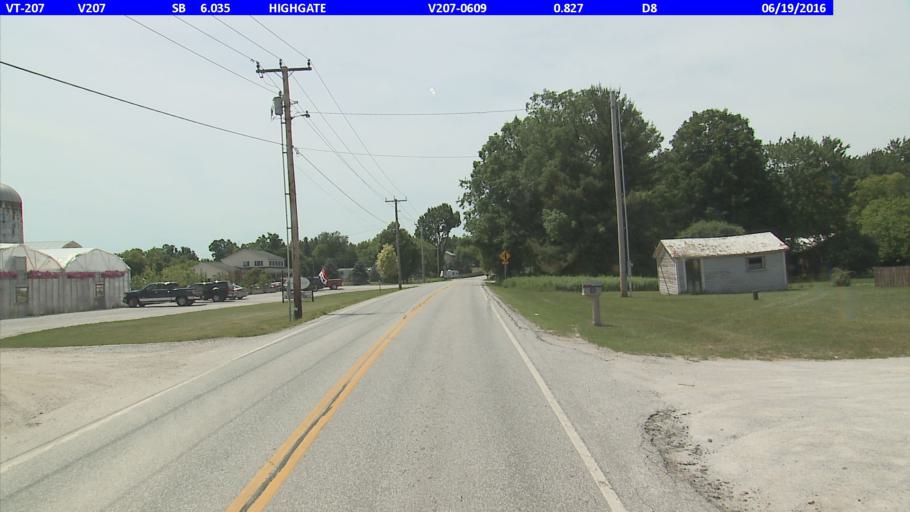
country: US
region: Vermont
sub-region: Franklin County
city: Swanton
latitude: 44.9228
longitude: -73.0525
